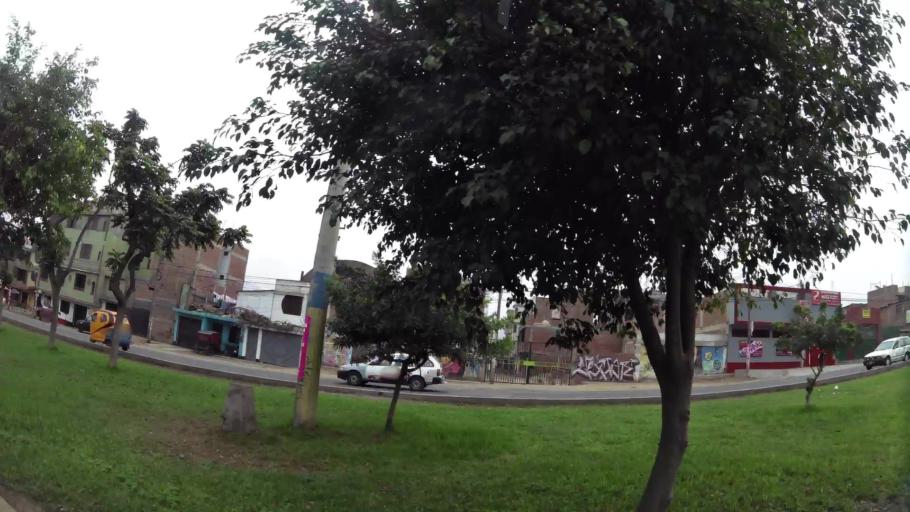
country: PE
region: Lima
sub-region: Lima
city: Independencia
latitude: -11.9858
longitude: -76.9951
